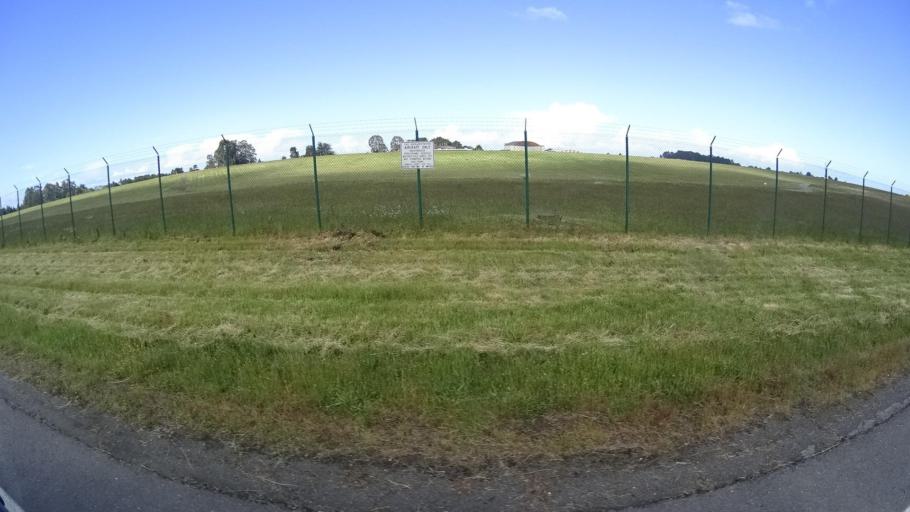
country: US
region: California
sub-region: Humboldt County
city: McKinleyville
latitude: 40.9714
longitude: -124.1007
